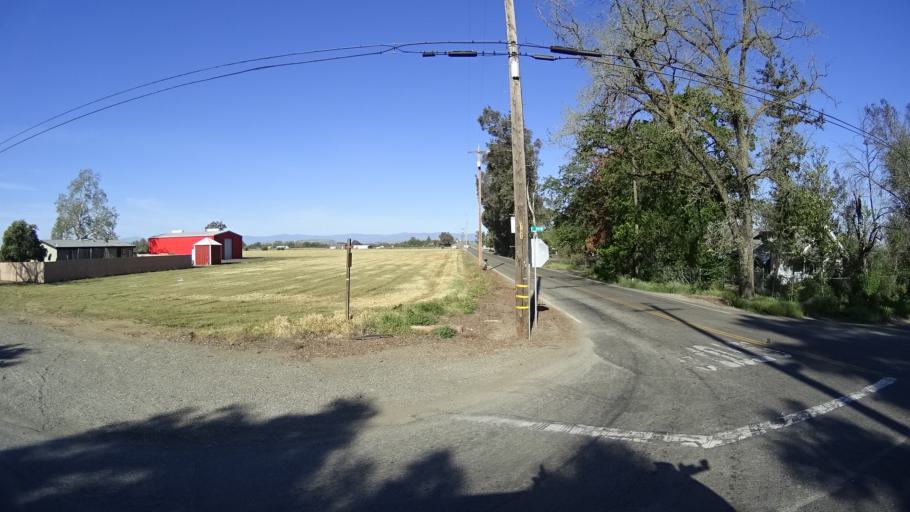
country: US
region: California
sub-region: Glenn County
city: Orland
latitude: 39.7836
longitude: -122.1976
